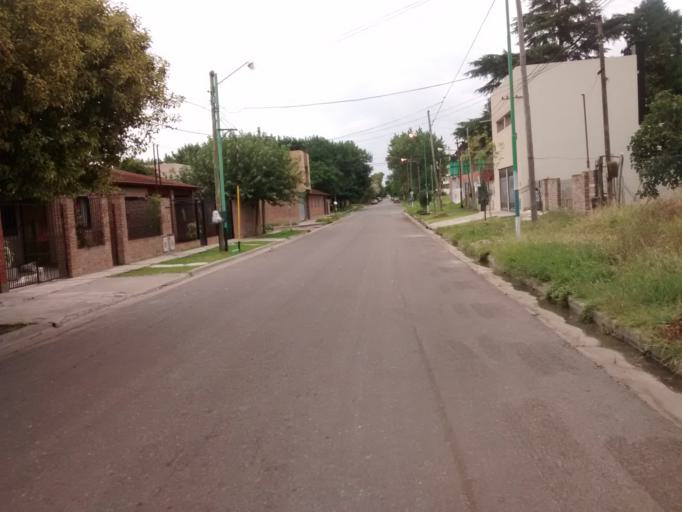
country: AR
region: Buenos Aires
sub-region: Partido de La Plata
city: La Plata
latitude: -34.9410
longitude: -57.9198
